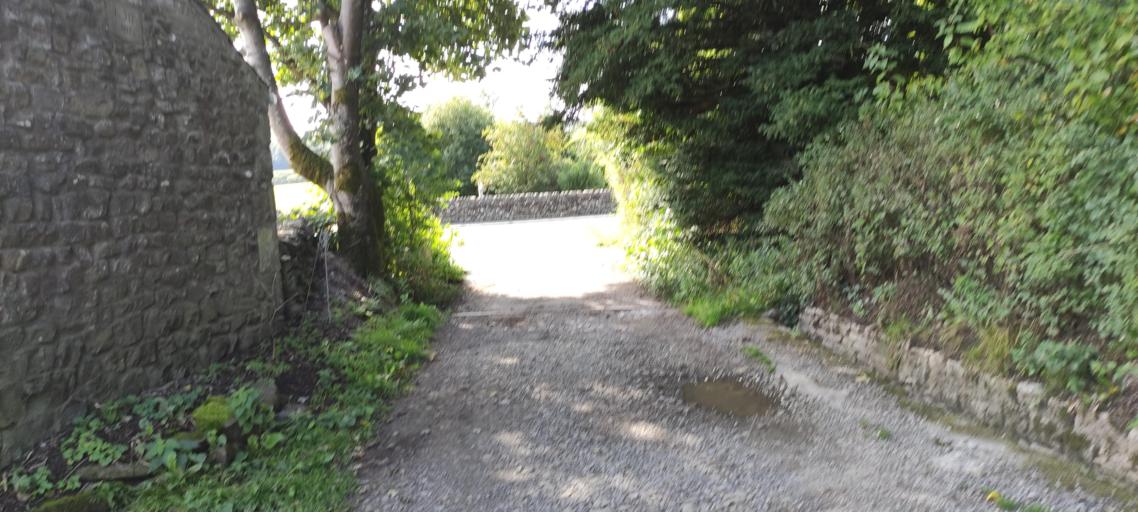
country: GB
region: England
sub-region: North Yorkshire
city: Settle
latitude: 54.1475
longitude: -2.2937
